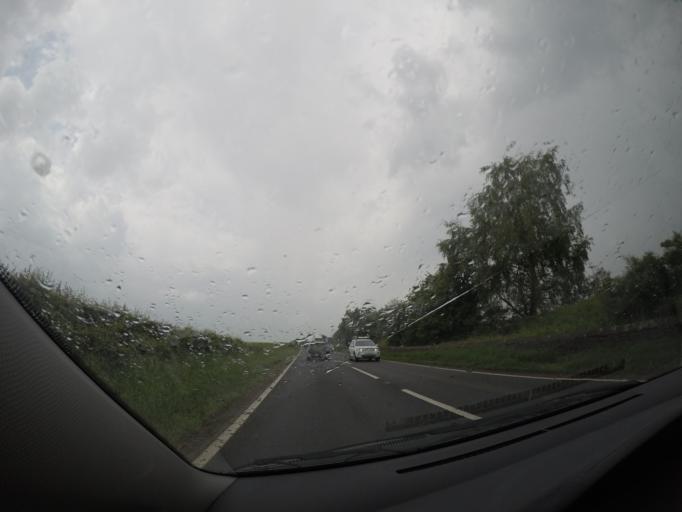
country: GB
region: England
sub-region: Cumbria
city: Appleby-in-Westmorland
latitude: 54.6125
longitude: -2.5471
